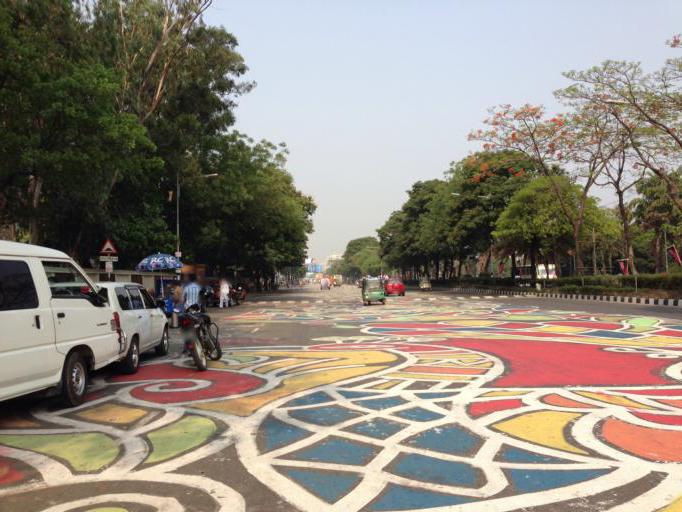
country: BD
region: Dhaka
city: Azimpur
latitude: 23.7584
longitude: 90.3814
